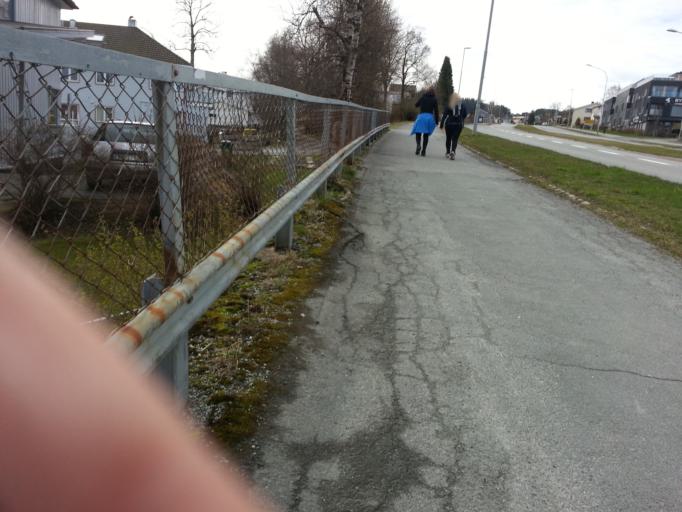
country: NO
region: Sor-Trondelag
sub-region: Trondheim
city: Trondheim
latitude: 63.4167
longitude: 10.3714
